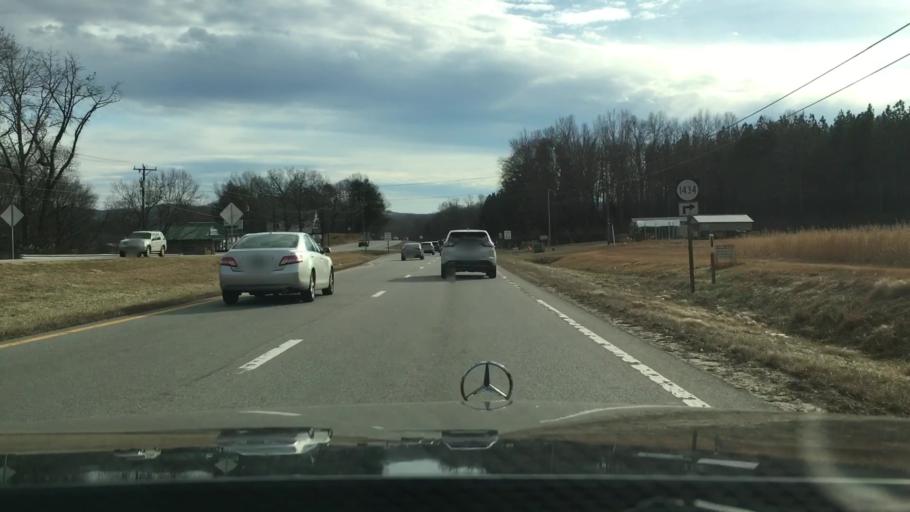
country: US
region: Virginia
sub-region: Pittsylvania County
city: Chatham
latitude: 36.7867
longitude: -79.3942
